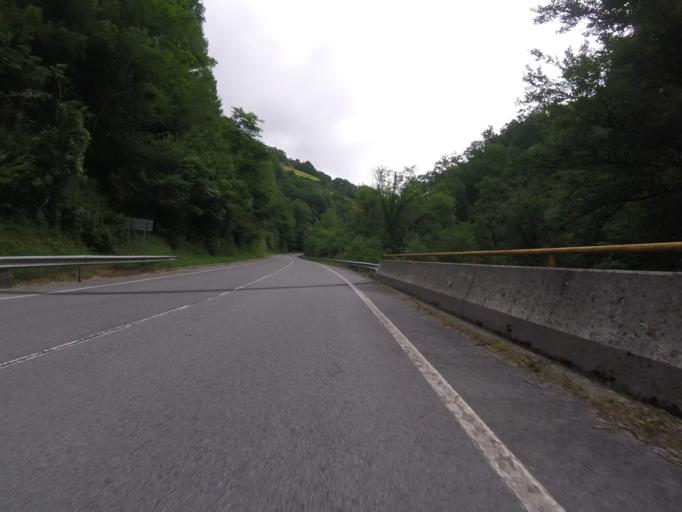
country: ES
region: Navarre
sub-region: Provincia de Navarra
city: Zubieta
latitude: 43.1155
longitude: -1.7584
